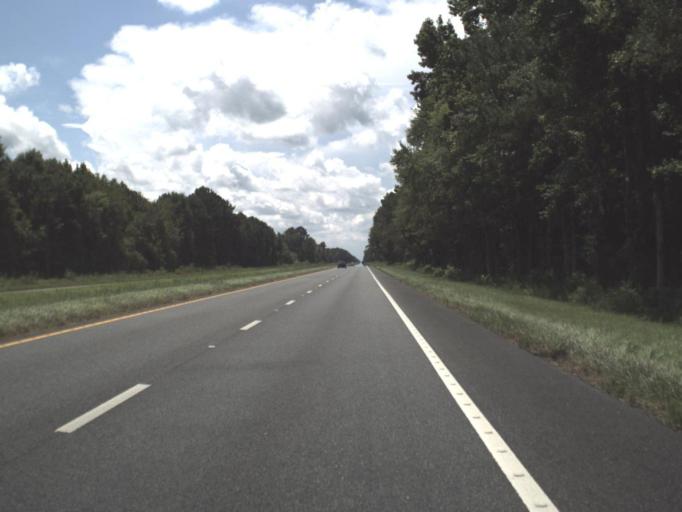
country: US
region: Florida
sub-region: Taylor County
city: Perry
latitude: 30.2718
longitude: -83.7197
